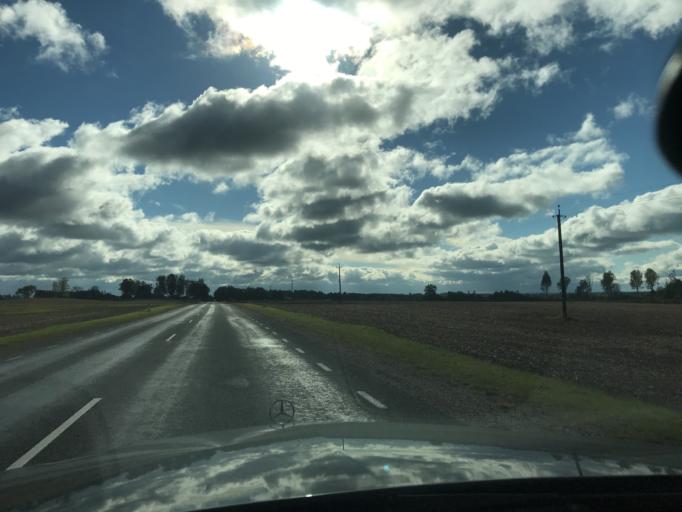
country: EE
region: Valgamaa
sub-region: Valga linn
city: Valga
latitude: 57.9700
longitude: 26.2621
